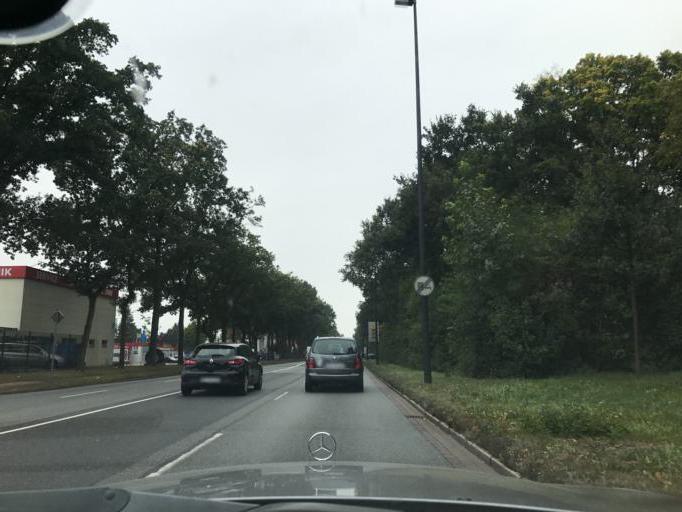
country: DE
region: Bremen
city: Bremen
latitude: 53.0577
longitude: 8.7955
